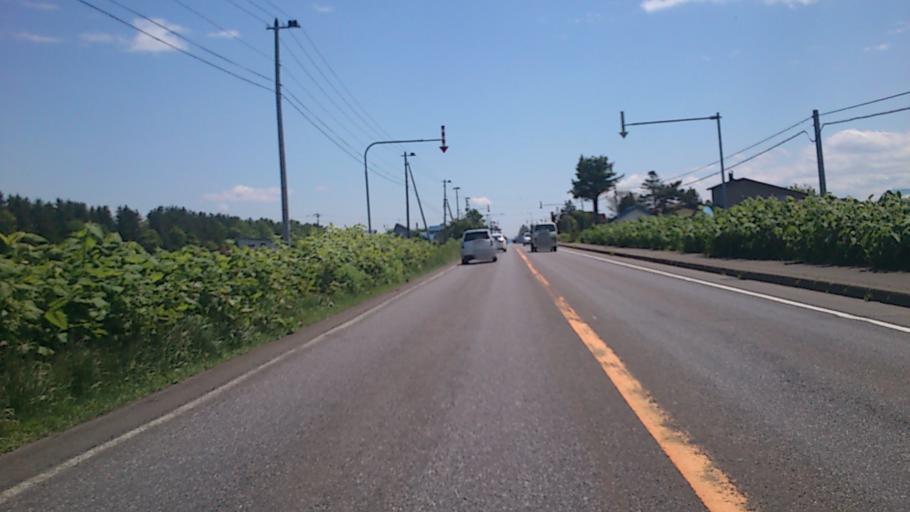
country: JP
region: Hokkaido
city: Nayoro
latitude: 44.2488
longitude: 142.3950
